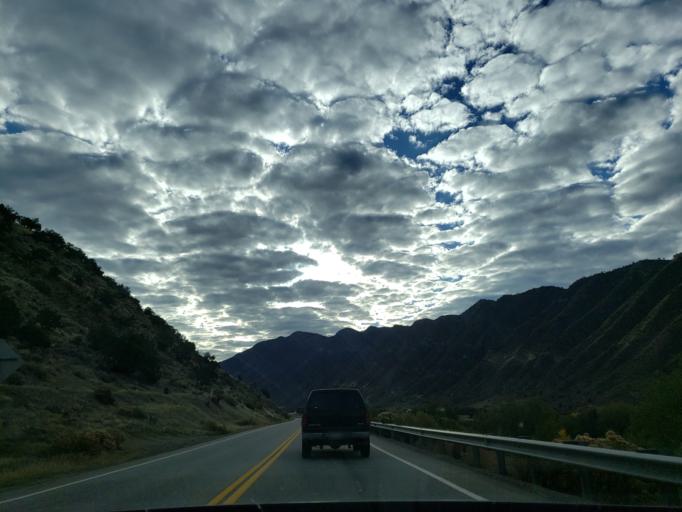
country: US
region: Colorado
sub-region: Garfield County
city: New Castle
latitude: 39.5702
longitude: -107.5226
